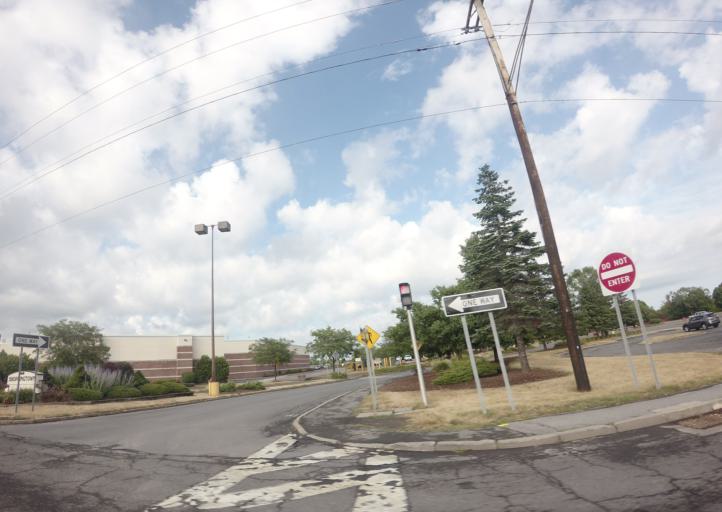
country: US
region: New York
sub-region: Onondaga County
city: East Syracuse
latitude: 43.0384
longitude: -76.0658
